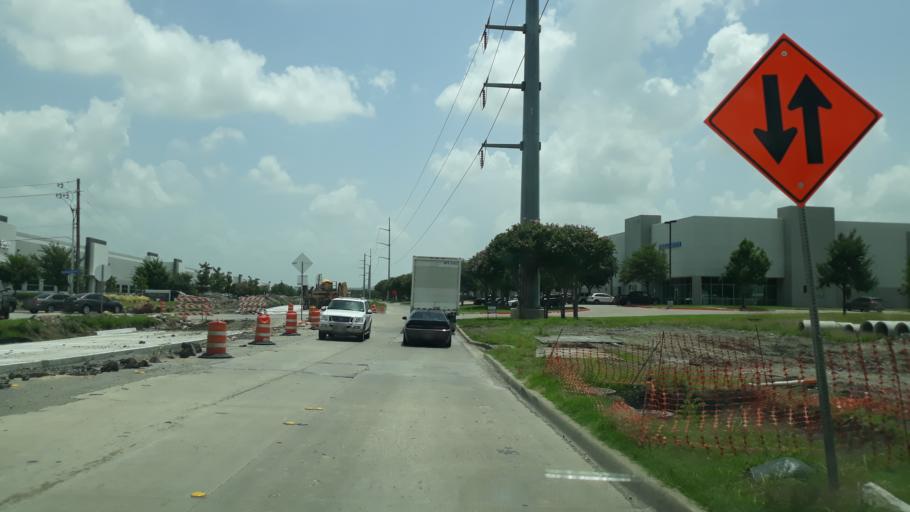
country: US
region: Texas
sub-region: Dallas County
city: Coppell
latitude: 32.9492
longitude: -97.0109
